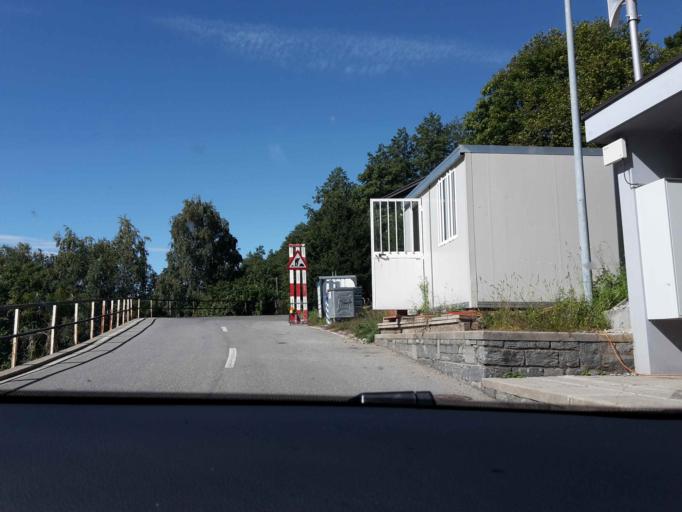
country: CH
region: Ticino
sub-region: Bellinzona District
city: Bellinzona
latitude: 46.1693
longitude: 9.0562
